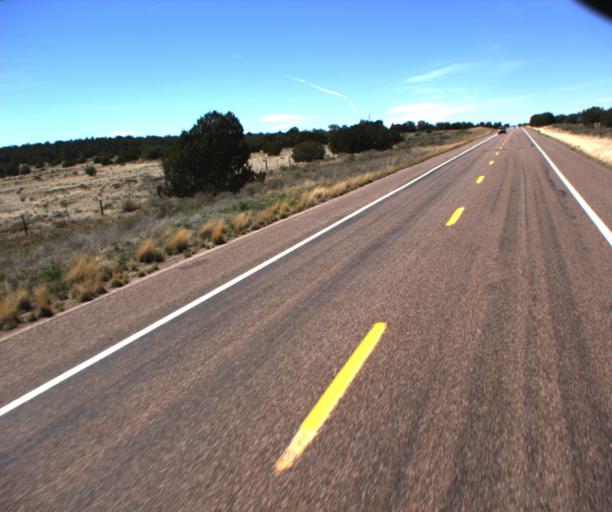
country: US
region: Arizona
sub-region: Mohave County
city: Peach Springs
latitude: 35.5076
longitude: -113.1837
